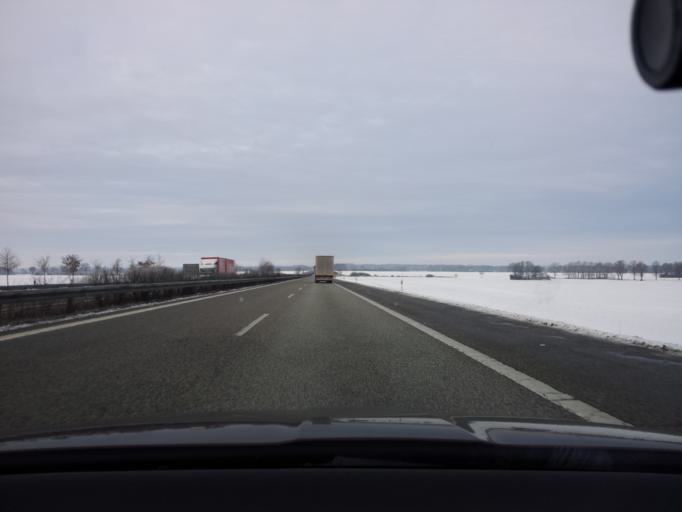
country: DE
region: Mecklenburg-Vorpommern
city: Hagenow
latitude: 53.4885
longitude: 11.1820
